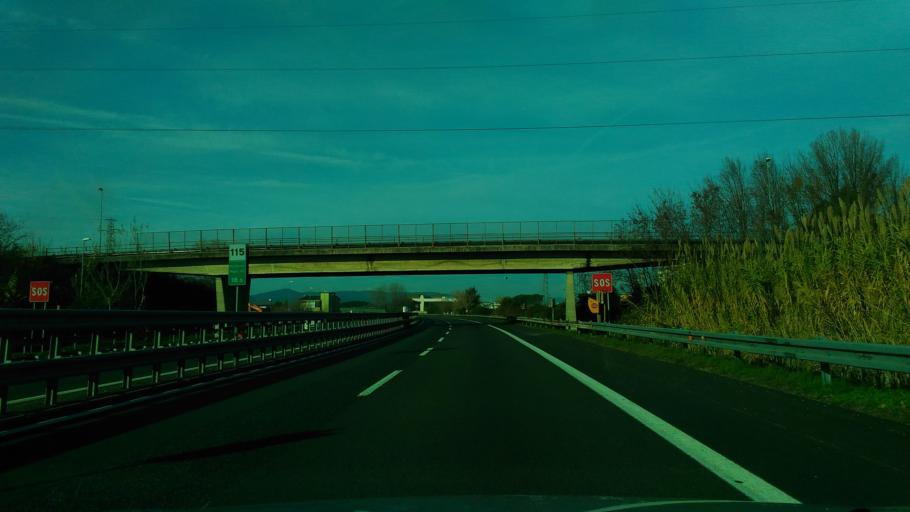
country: IT
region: Tuscany
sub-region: Provincia di Massa-Carrara
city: Carrara
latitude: 44.0314
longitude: 10.0859
